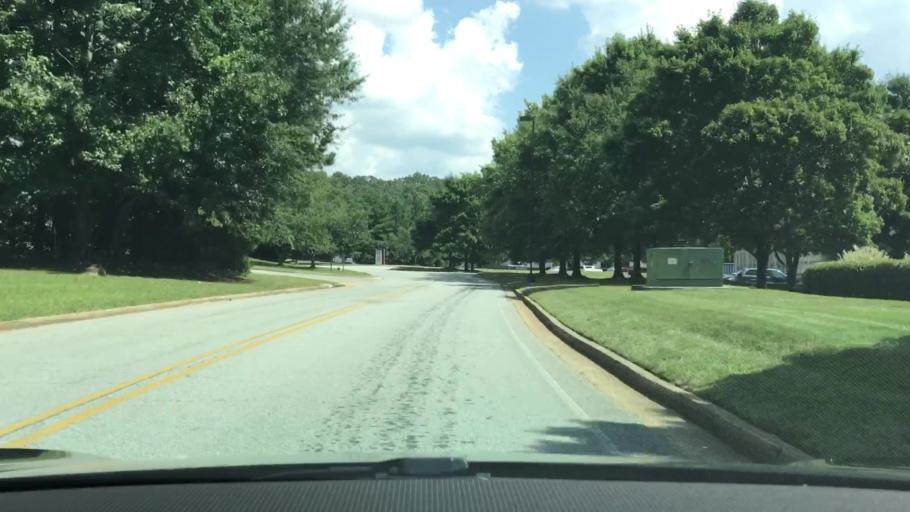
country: US
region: Georgia
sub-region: Gwinnett County
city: Buford
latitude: 34.1007
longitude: -84.0064
